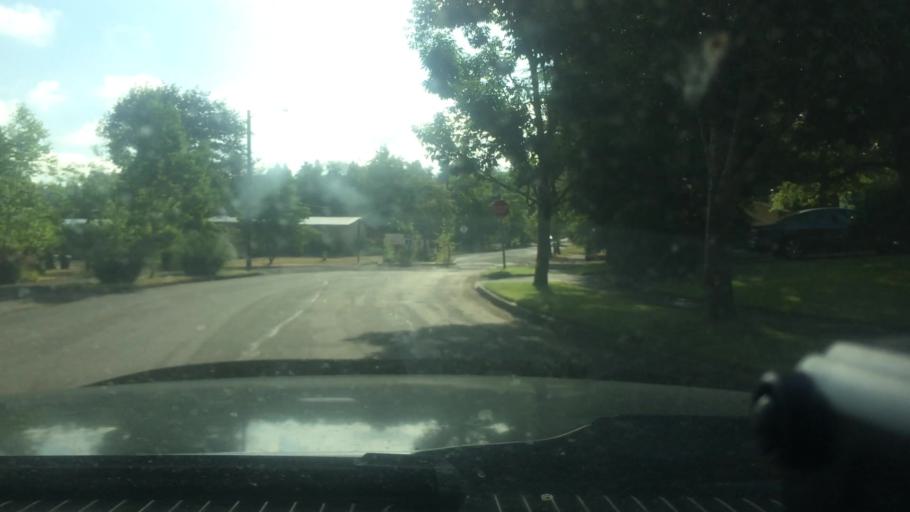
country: US
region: Oregon
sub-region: Lane County
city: Eugene
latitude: 44.0297
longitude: -123.1092
